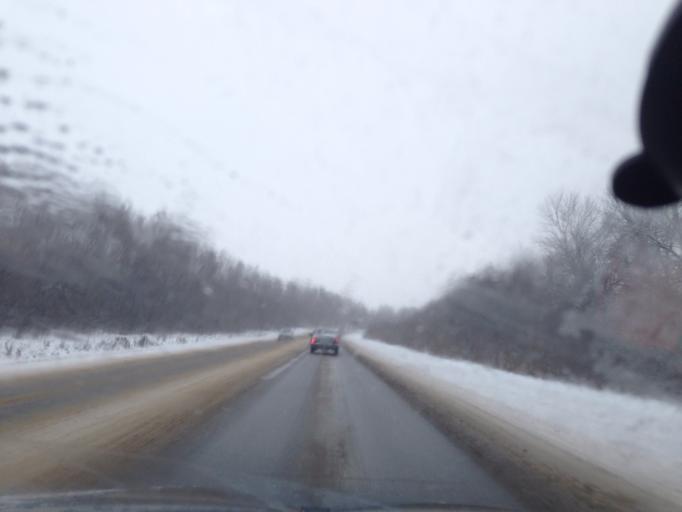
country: RU
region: Tula
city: Bolokhovo
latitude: 54.1026
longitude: 37.7631
